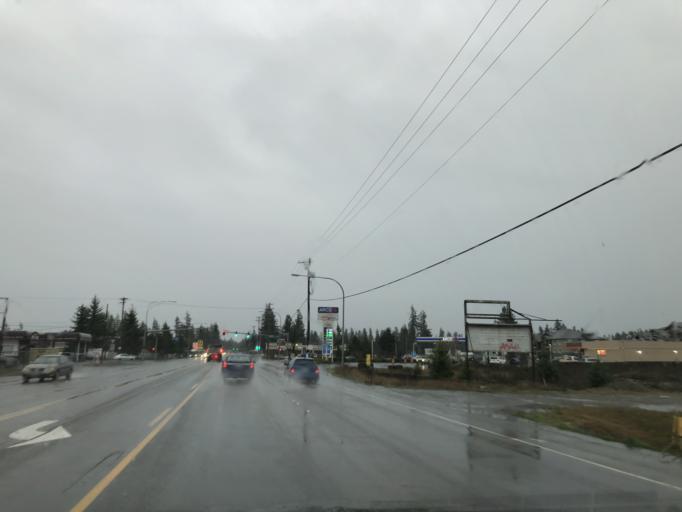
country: US
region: Washington
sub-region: Pierce County
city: Spanaway
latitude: 47.0747
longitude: -122.4231
